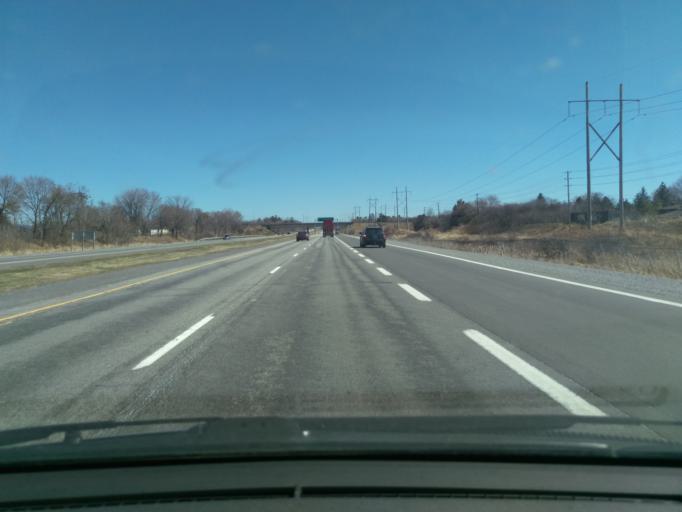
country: CA
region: Quebec
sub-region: Outaouais
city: Gatineau
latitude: 45.4717
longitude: -75.5388
